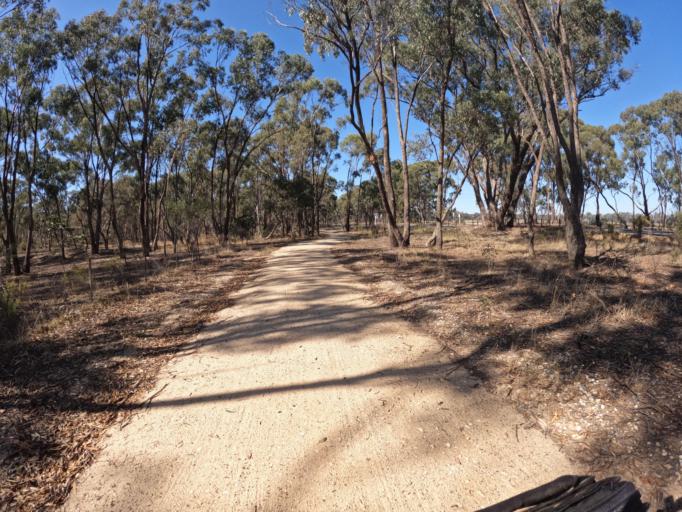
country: AU
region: Victoria
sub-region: Greater Bendigo
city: Epsom
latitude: -36.7884
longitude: 144.5279
